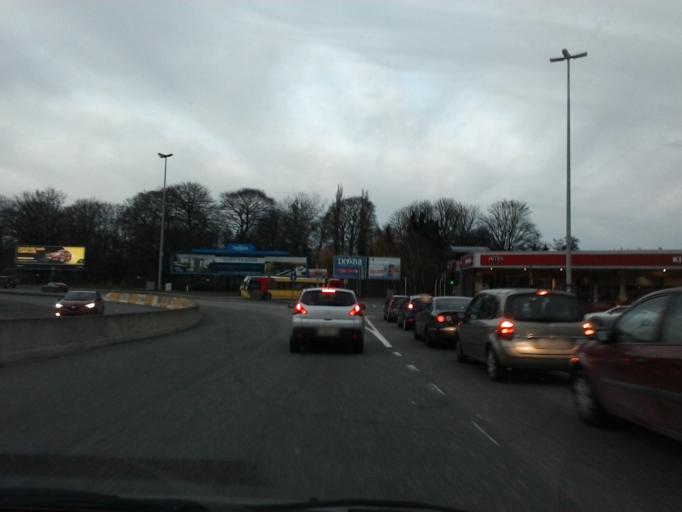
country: BE
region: Wallonia
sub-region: Province de Liege
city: Liege
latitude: 50.6152
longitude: 5.6013
